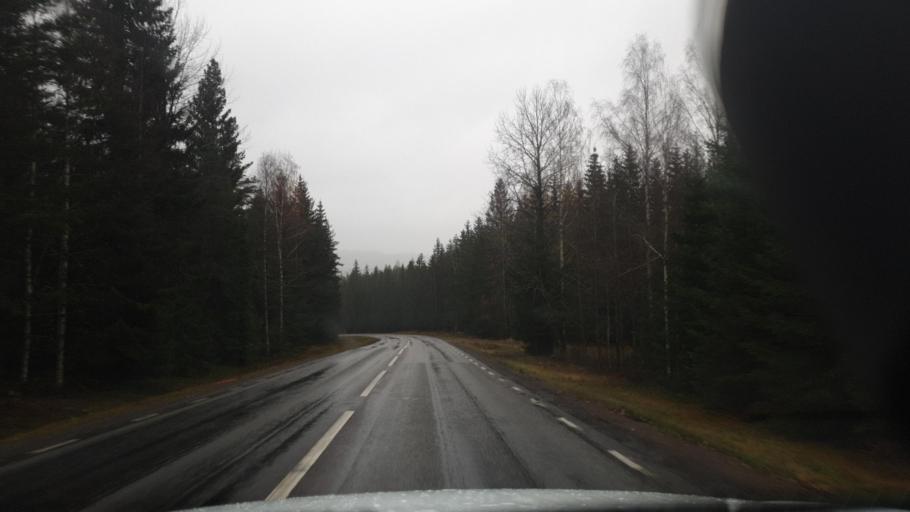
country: SE
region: Vaermland
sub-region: Sunne Kommun
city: Sunne
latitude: 59.7061
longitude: 13.1063
